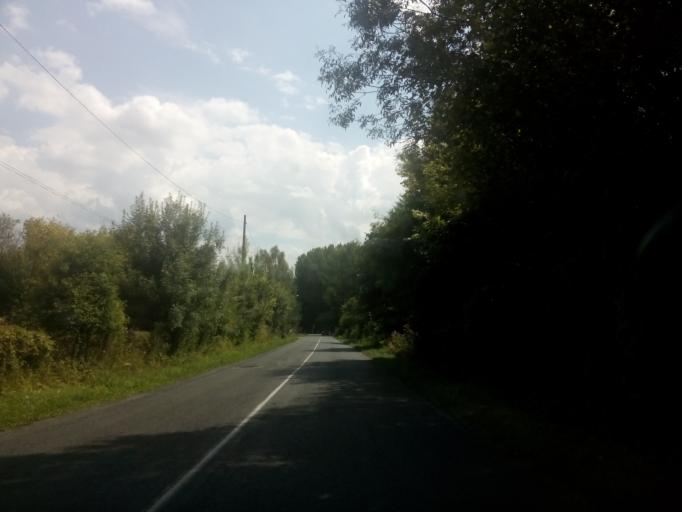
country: FR
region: Centre
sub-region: Departement d'Indre-et-Loire
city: Azay-le-Rideau
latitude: 47.2660
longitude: 0.4425
